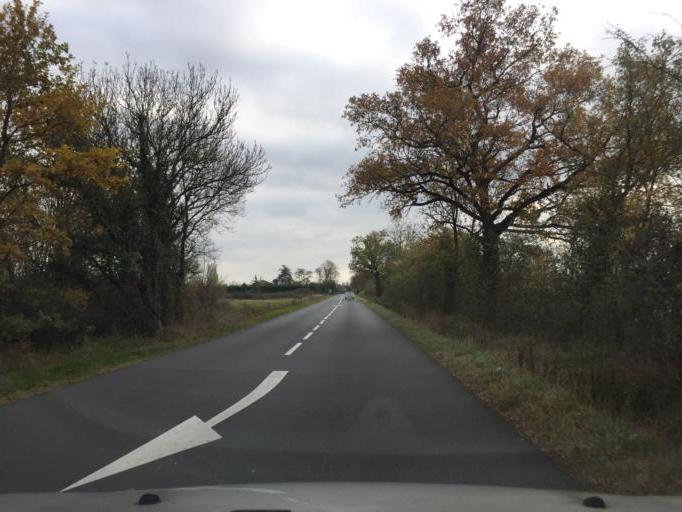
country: FR
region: Rhone-Alpes
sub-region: Departement de l'Ain
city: Sainte-Euphemie
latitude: 45.9561
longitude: 4.8027
